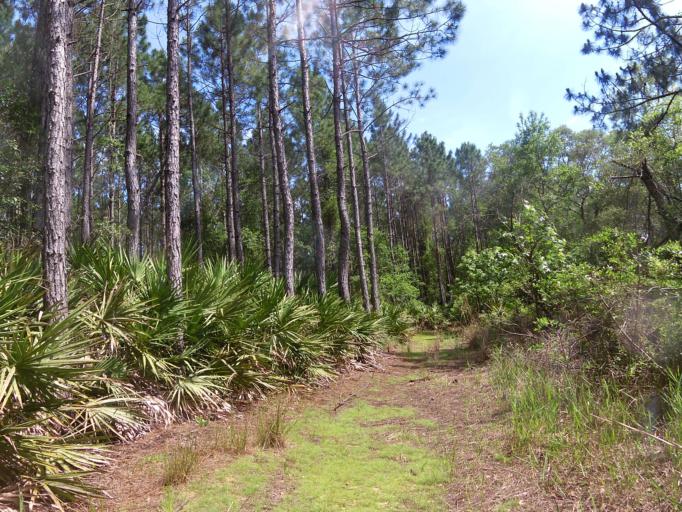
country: US
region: Florida
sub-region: Nassau County
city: Yulee
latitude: 30.4892
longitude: -81.5005
